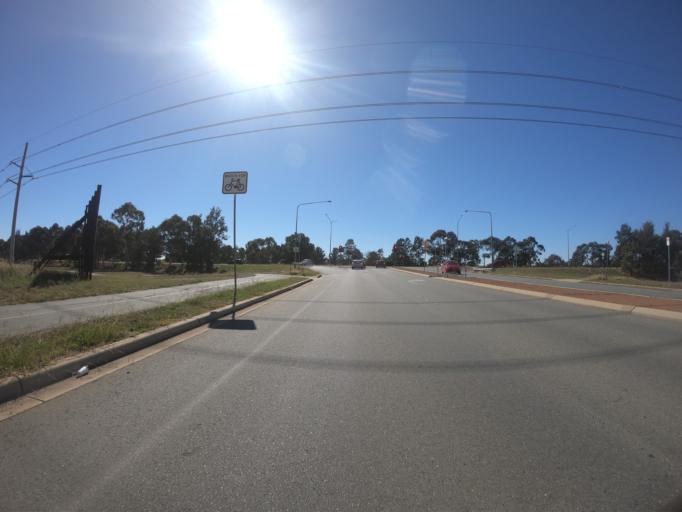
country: AU
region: Australian Capital Territory
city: Kaleen
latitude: -35.2402
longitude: 149.1031
